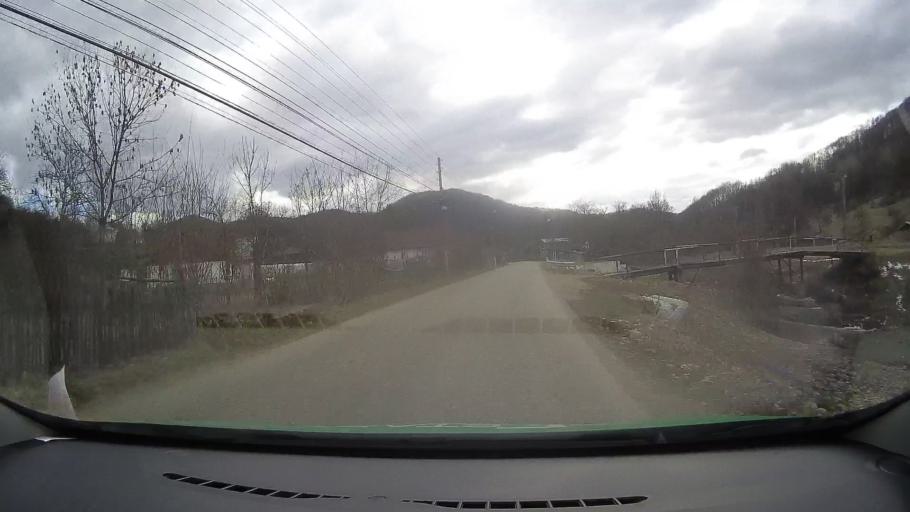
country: RO
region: Dambovita
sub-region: Comuna Visinesti
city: Visinesti
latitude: 45.0992
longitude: 25.5707
